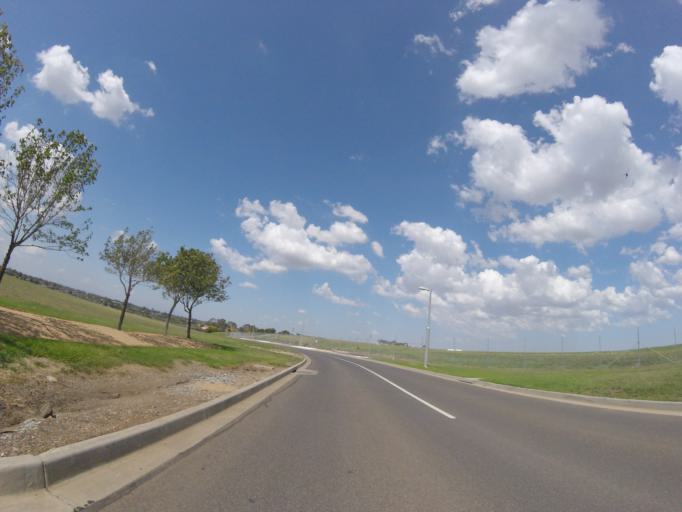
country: AU
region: Victoria
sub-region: Moreland
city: Gowanbrae
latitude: -37.7193
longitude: 144.8995
